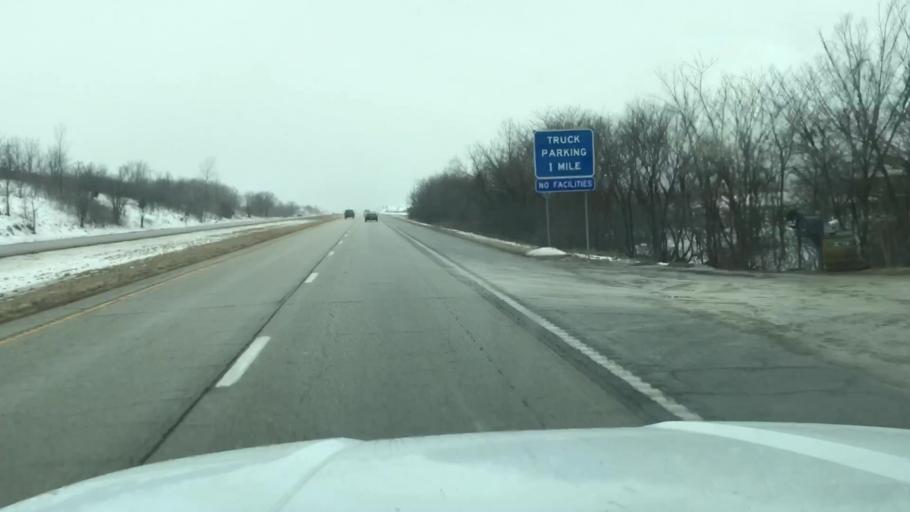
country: US
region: Missouri
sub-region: Clinton County
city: Gower
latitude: 39.7477
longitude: -94.6760
